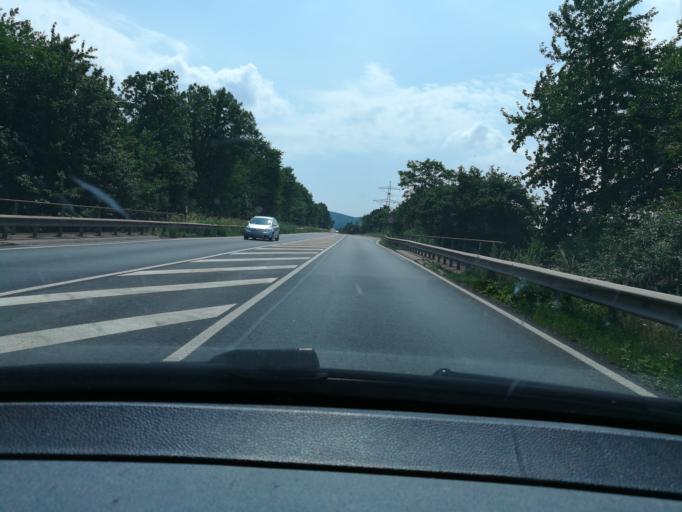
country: DE
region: North Rhine-Westphalia
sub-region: Regierungsbezirk Detmold
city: Minden
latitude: 52.2801
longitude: 8.9677
